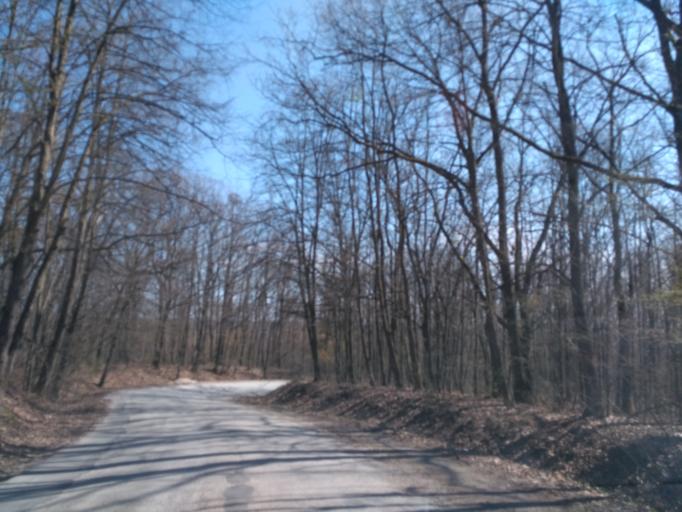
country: SK
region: Kosicky
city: Moldava nad Bodvou
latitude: 48.6474
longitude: 20.9986
